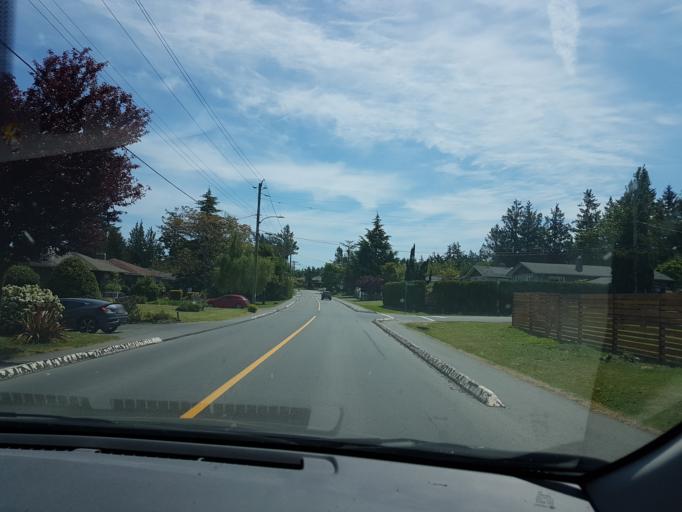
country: CA
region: British Columbia
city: Oak Bay
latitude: 48.4879
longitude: -123.3128
